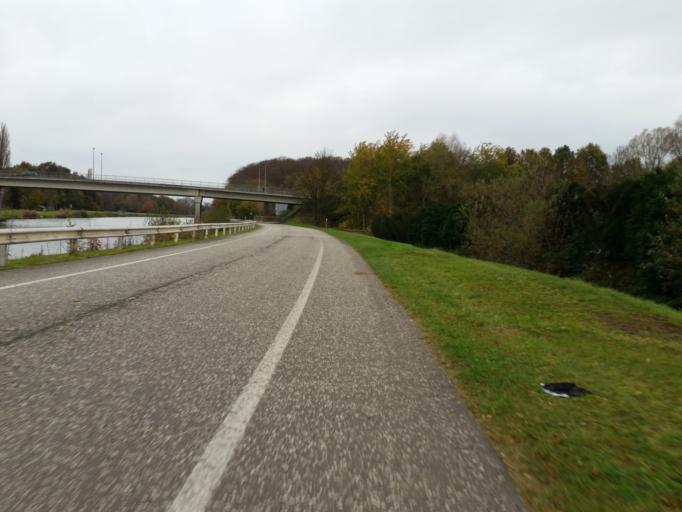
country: BE
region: Flanders
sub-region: Provincie Antwerpen
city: Lier
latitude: 51.1325
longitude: 4.5928
